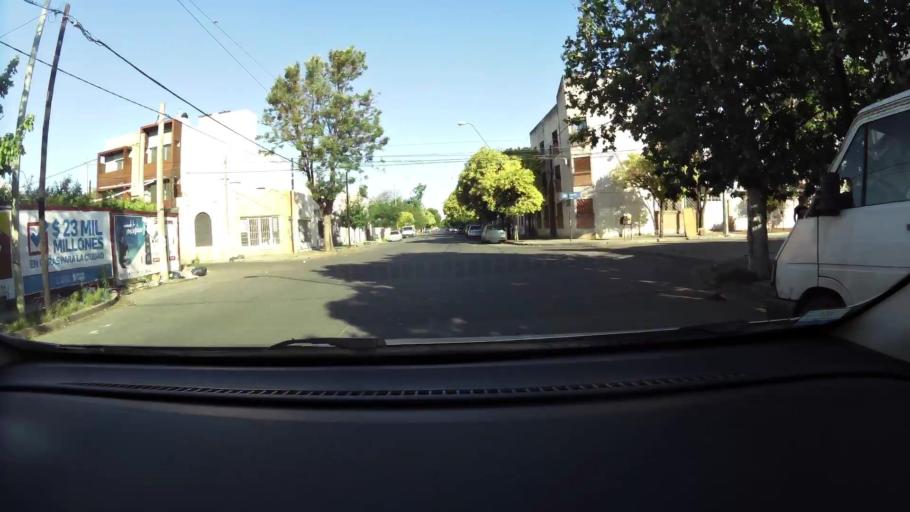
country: AR
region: Cordoba
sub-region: Departamento de Capital
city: Cordoba
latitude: -31.3939
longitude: -64.1796
